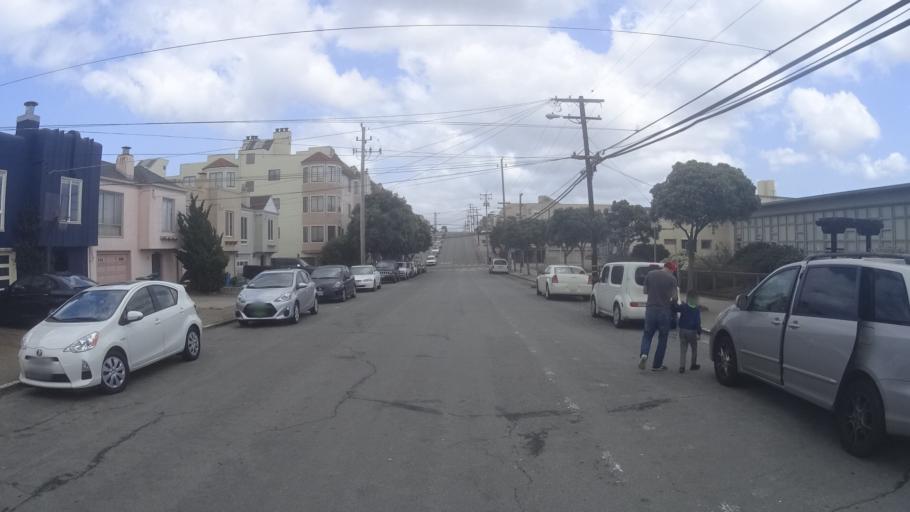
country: US
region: California
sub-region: San Mateo County
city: Daly City
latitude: 37.7374
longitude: -122.5000
